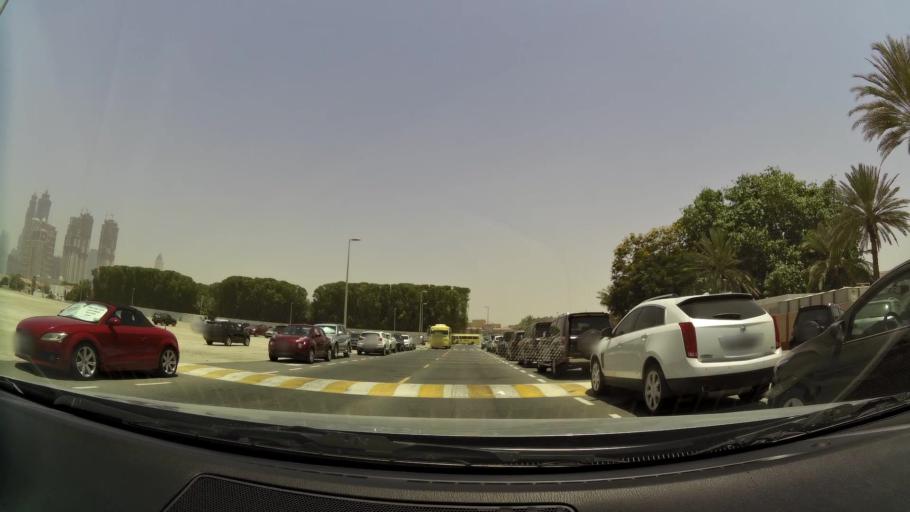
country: AE
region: Dubai
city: Dubai
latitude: 25.1805
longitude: 55.2434
